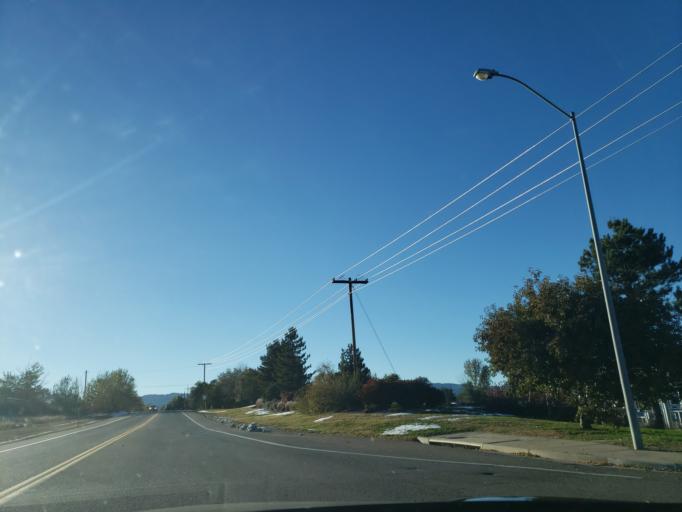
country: US
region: Colorado
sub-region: Larimer County
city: Fort Collins
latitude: 40.4948
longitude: -105.0664
